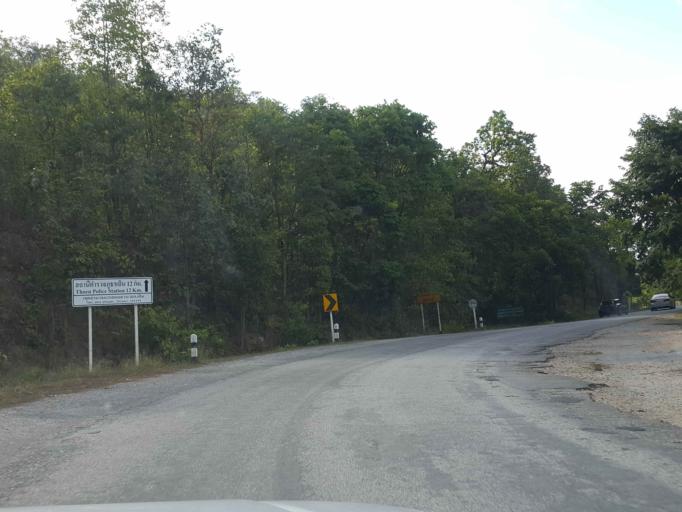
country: TH
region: Lampang
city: Thoen
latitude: 17.6220
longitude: 99.3137
